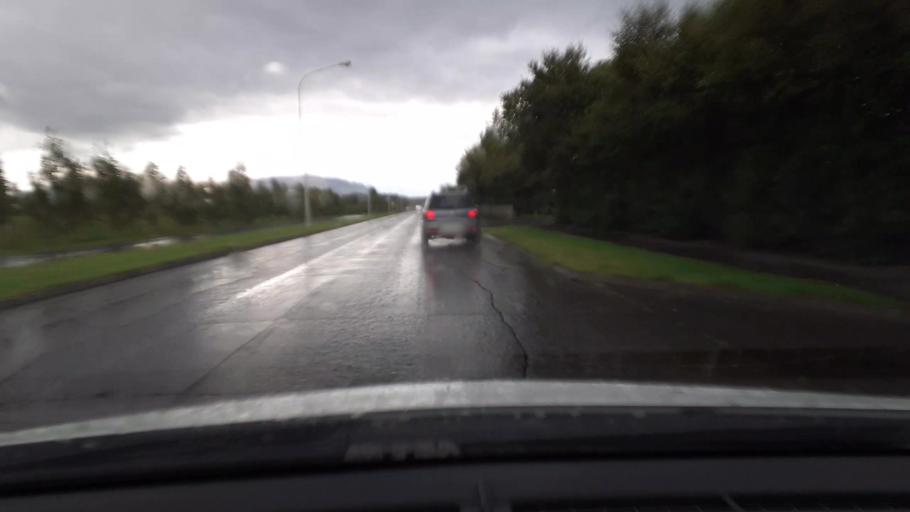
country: IS
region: West
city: Akranes
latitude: 64.3179
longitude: -22.0463
